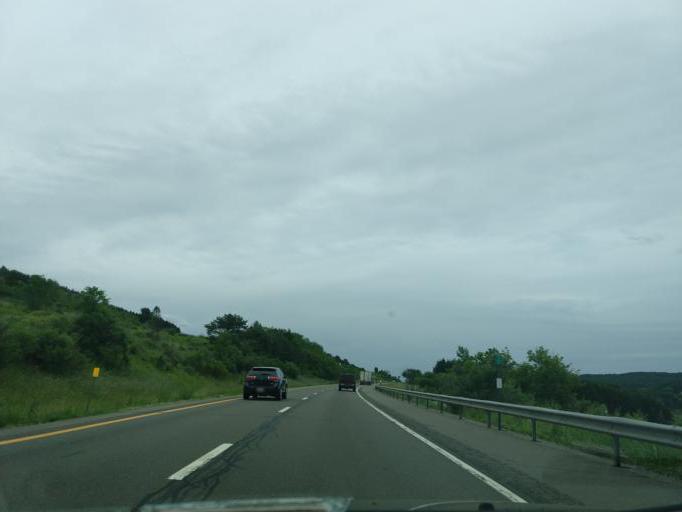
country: US
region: New York
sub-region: Chenango County
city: Lakeview
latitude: 42.4248
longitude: -76.0190
